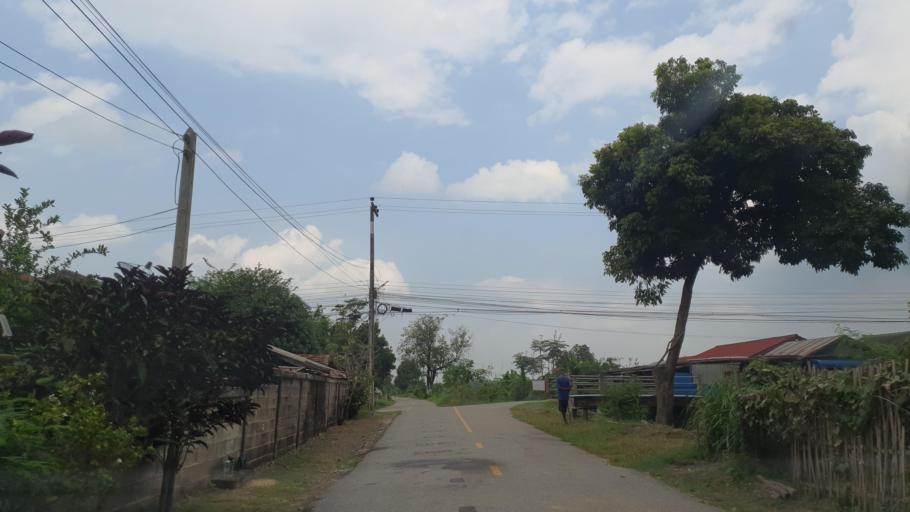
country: TH
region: Sukhothai
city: Thung Saliam
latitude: 17.3192
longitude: 99.5112
